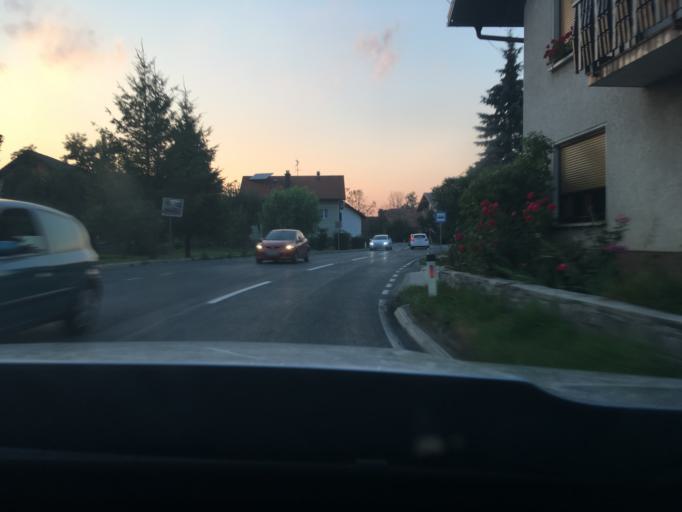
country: SI
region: Ribnica
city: Ribnica
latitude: 45.7203
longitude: 14.7441
